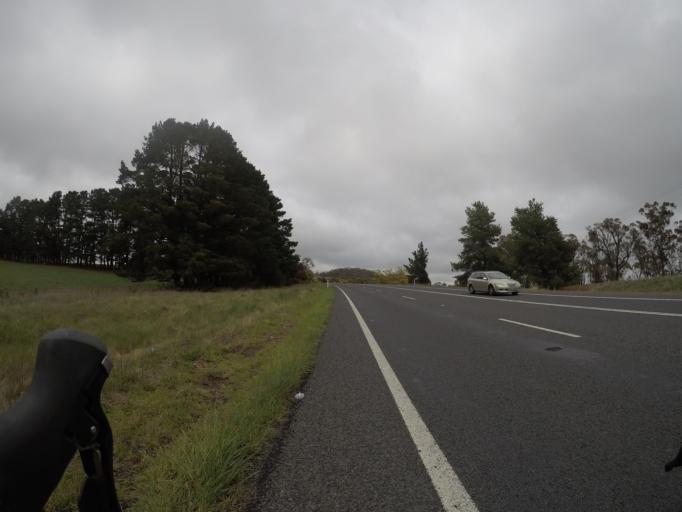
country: AU
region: New South Wales
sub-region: Lithgow
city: Portland
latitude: -33.4501
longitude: 149.9889
